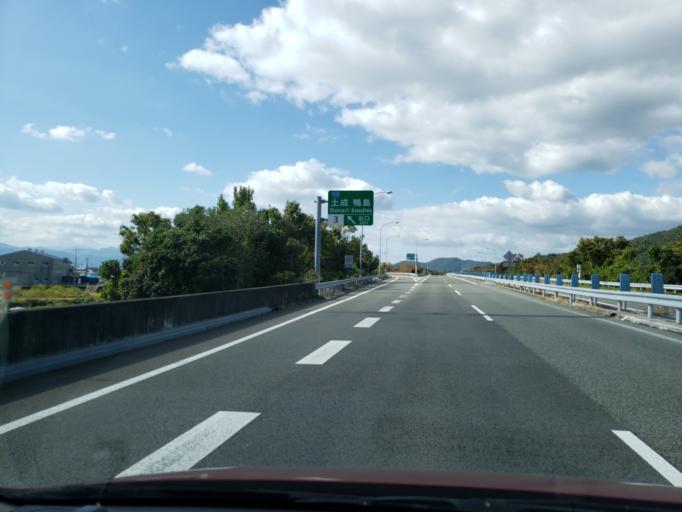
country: JP
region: Tokushima
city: Kamojimacho-jogejima
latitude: 34.1218
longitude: 134.3589
